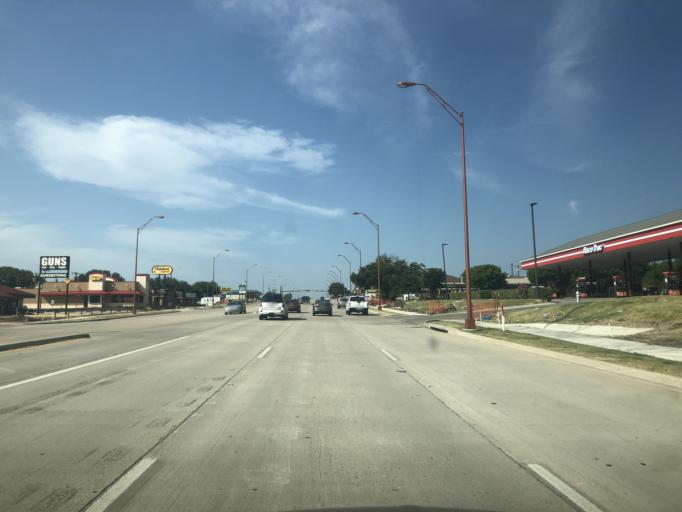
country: US
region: Texas
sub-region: Tarrant County
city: Benbrook
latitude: 32.6765
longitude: -97.4666
